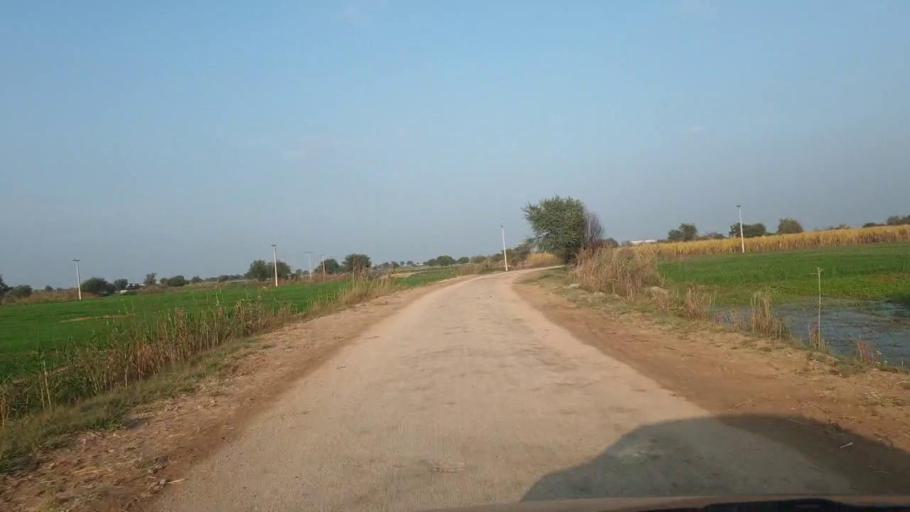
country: PK
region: Sindh
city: Berani
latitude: 25.8575
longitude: 68.7366
